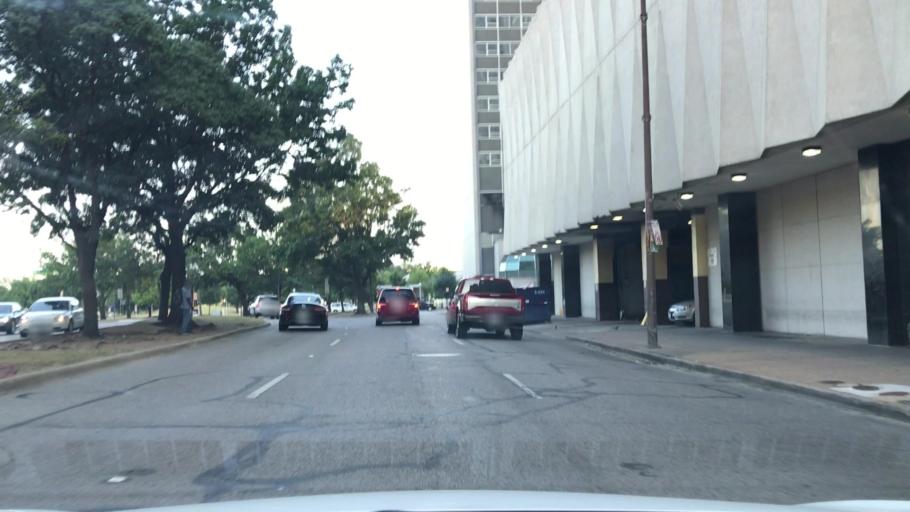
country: US
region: Texas
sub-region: Dallas County
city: Dallas
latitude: 32.7856
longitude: -96.7949
